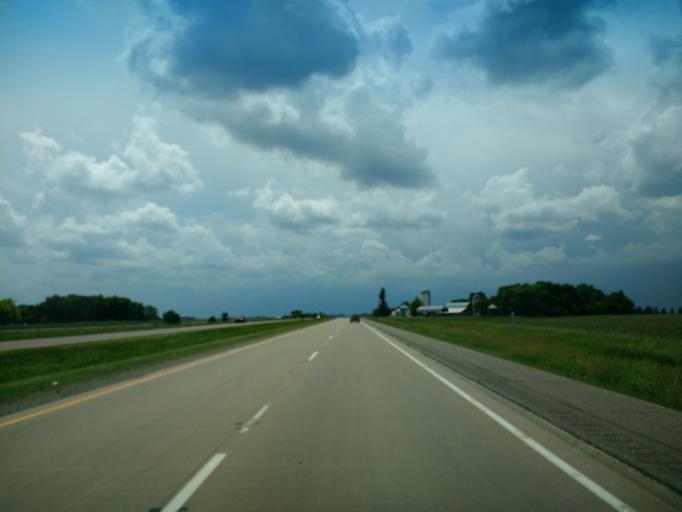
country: US
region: Minnesota
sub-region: Nobles County
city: Worthington
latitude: 43.6909
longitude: -95.4838
